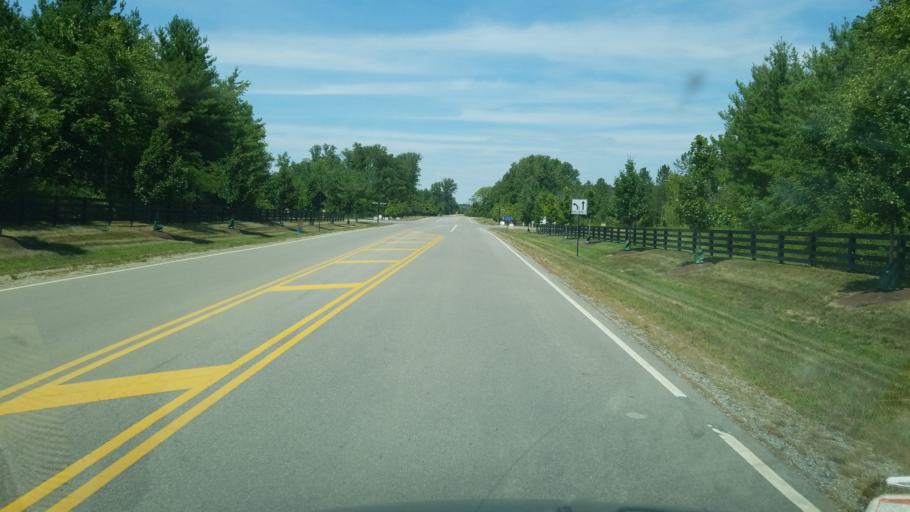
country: US
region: Ohio
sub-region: Union County
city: New California
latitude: 40.1784
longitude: -83.1899
